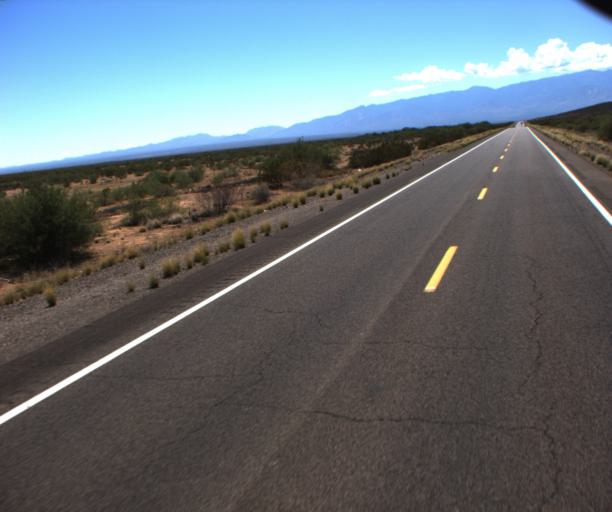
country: US
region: Arizona
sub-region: Graham County
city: Safford
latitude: 32.8077
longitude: -109.5096
